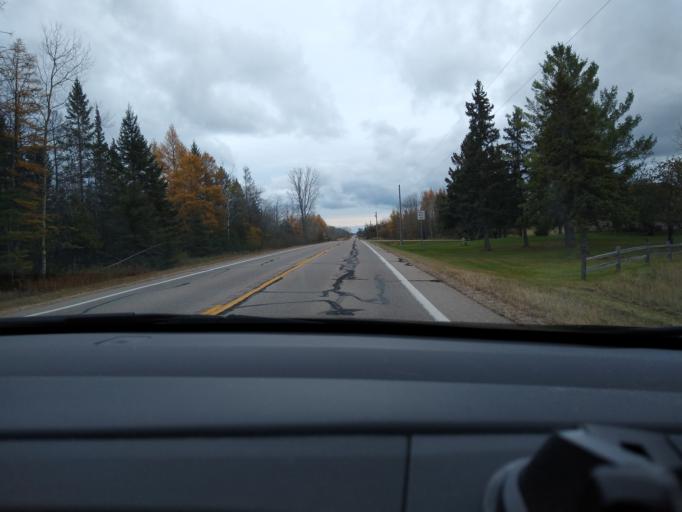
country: US
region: Michigan
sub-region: Delta County
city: Escanaba
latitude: 45.7770
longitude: -87.3214
